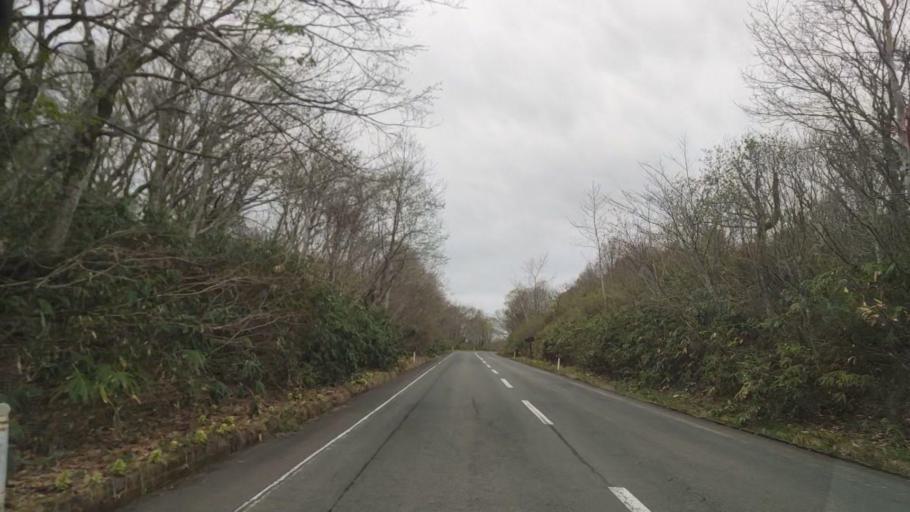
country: JP
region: Akita
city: Hanawa
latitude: 40.4077
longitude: 140.8587
